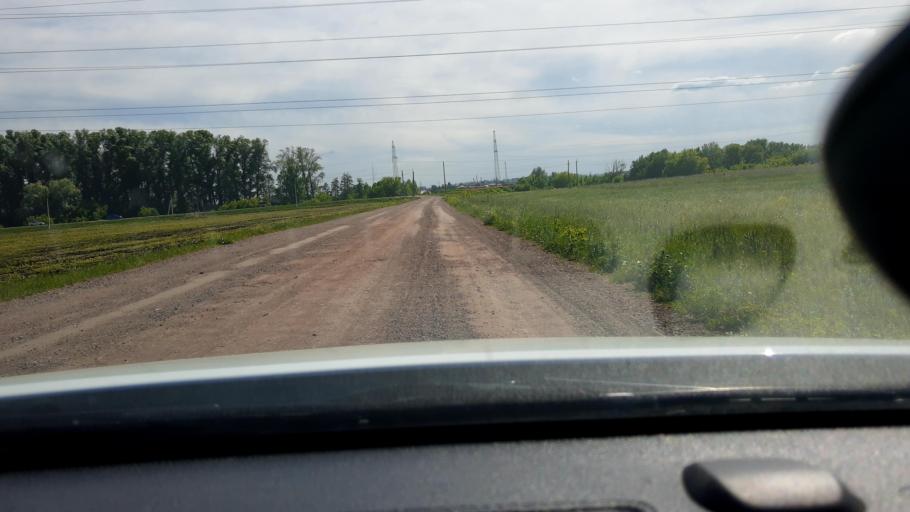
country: RU
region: Bashkortostan
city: Avdon
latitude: 54.4348
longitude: 55.8202
